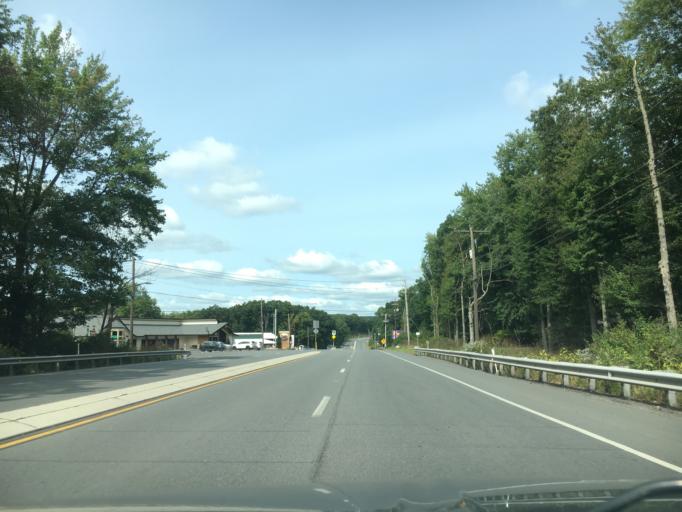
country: US
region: Pennsylvania
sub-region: Schuylkill County
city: Hometown
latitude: 40.8353
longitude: -75.9912
